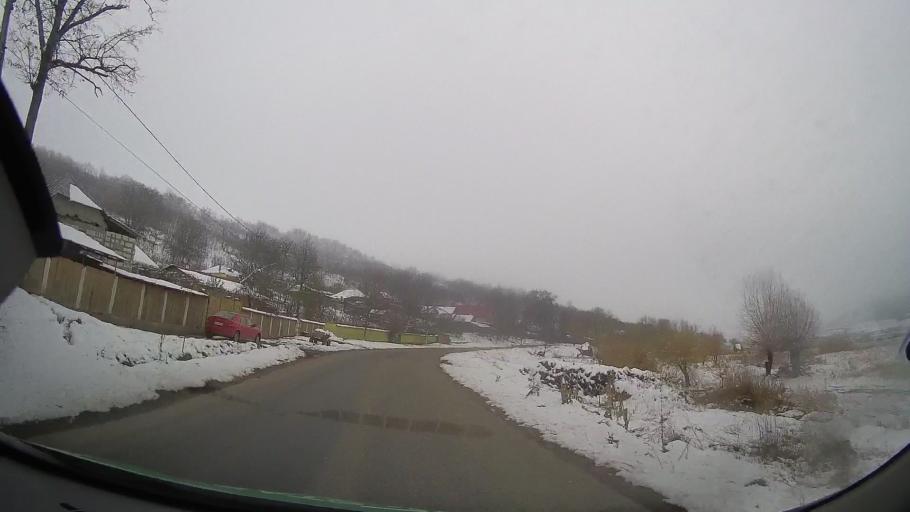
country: RO
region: Bacau
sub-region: Comuna Vultureni
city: Vultureni
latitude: 46.3597
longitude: 27.2886
